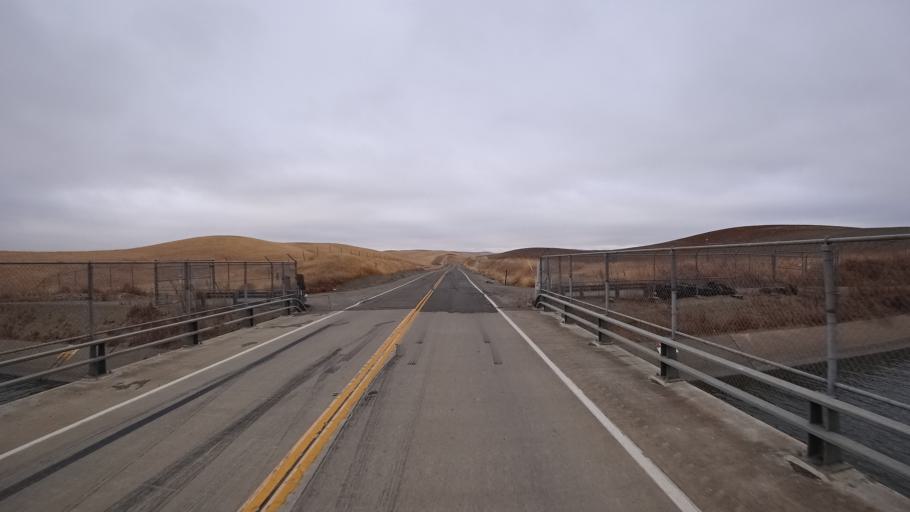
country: US
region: California
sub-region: Yolo County
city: Dunnigan
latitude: 38.8809
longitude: -121.9977
